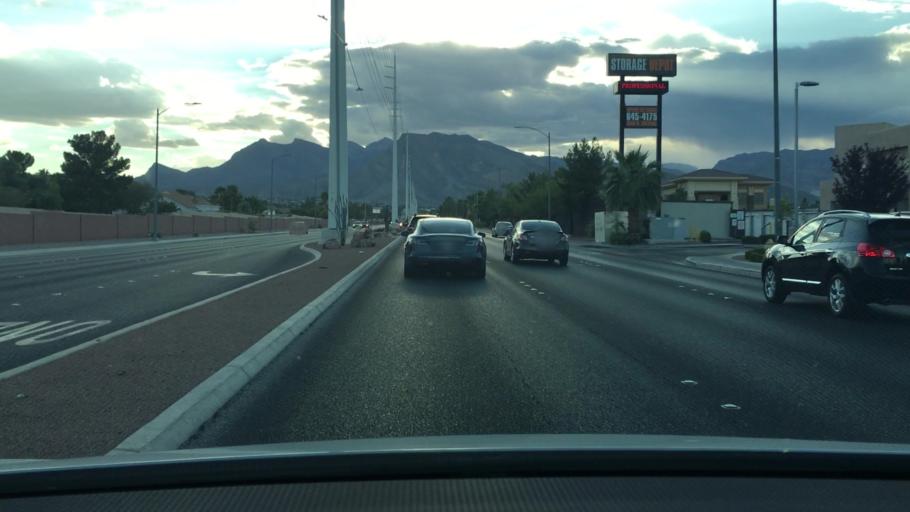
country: US
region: Nevada
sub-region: Clark County
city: Summerlin South
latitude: 36.2187
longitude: -115.2814
